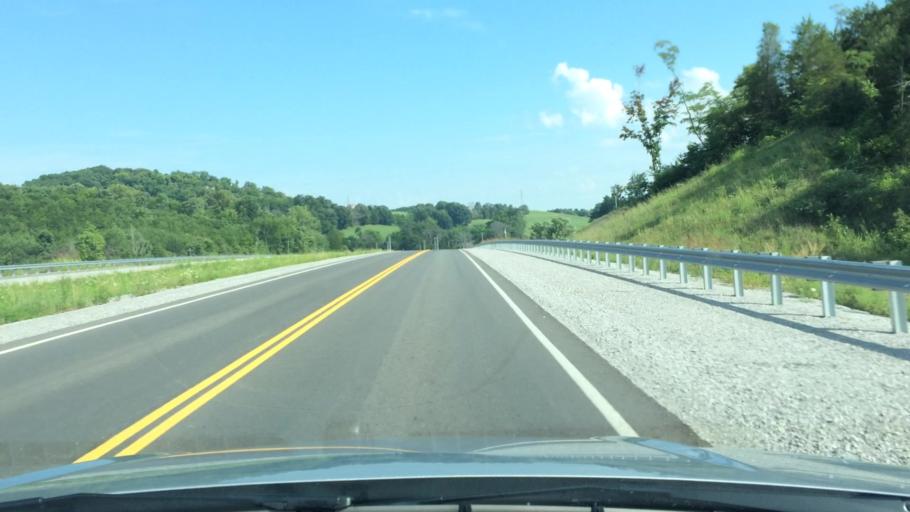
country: US
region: Tennessee
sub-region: Jefferson County
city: White Pine
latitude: 36.1373
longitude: -83.3403
